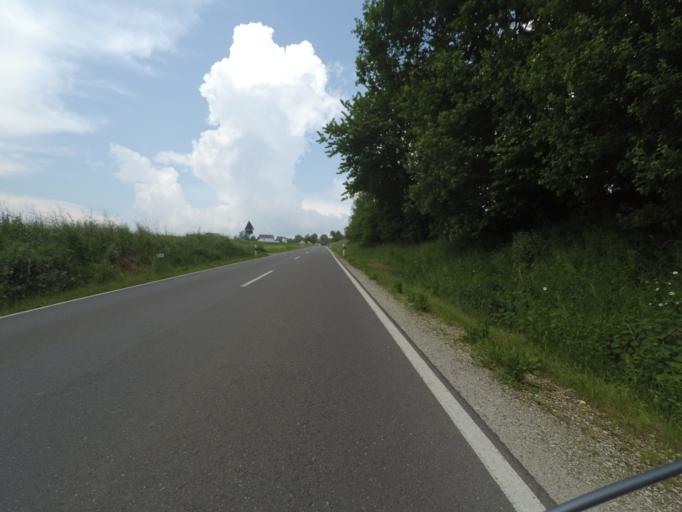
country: DE
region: Rheinland-Pfalz
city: Beltheim
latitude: 50.1009
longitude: 7.4633
